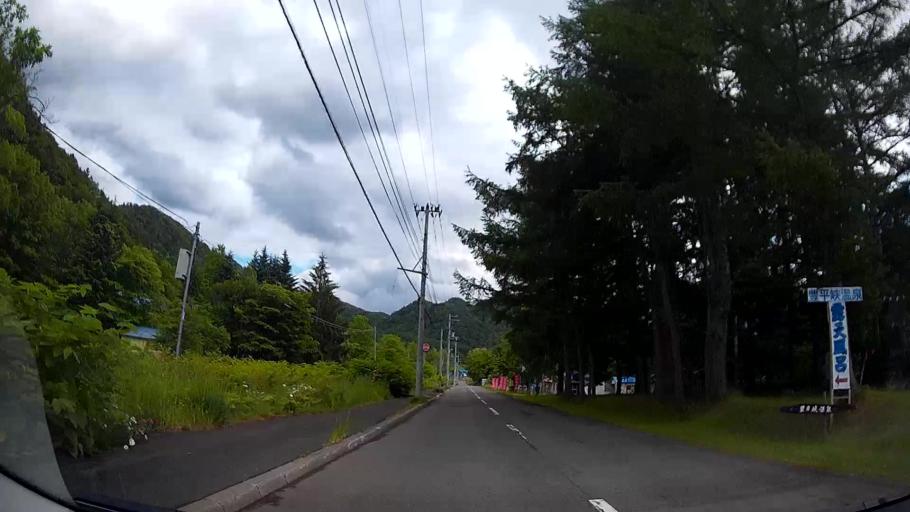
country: JP
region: Hokkaido
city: Sapporo
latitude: 42.9516
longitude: 141.1520
